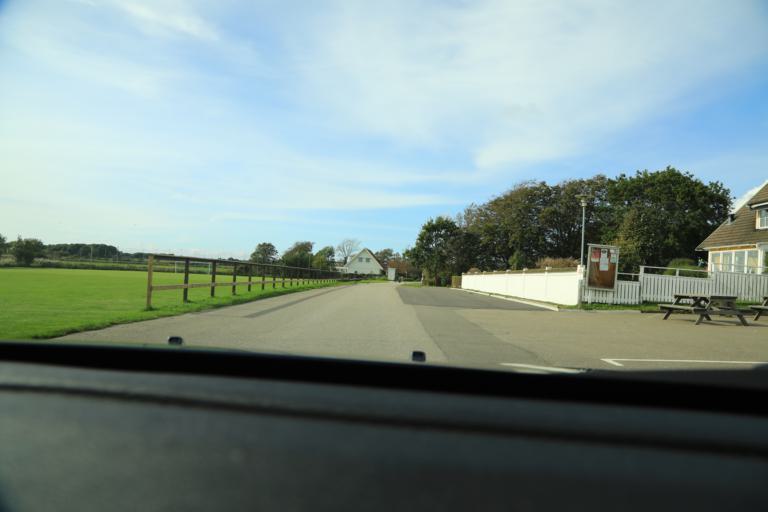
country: SE
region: Halland
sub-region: Varbergs Kommun
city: Traslovslage
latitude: 57.0403
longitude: 12.3214
